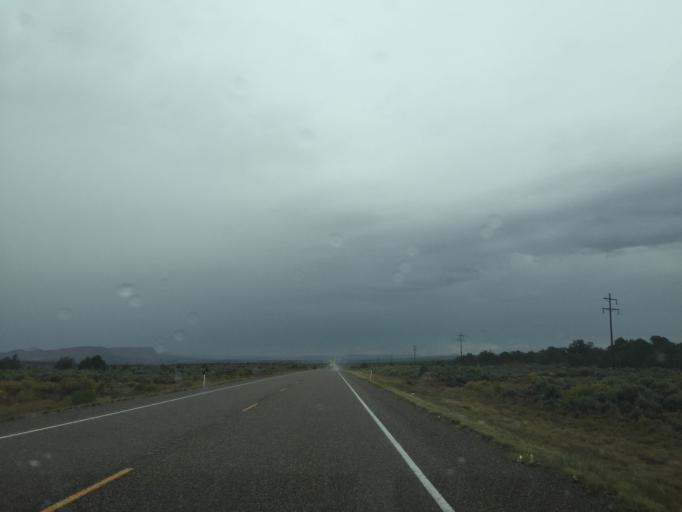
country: US
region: Utah
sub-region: Kane County
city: Kanab
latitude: 37.0877
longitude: -112.1507
